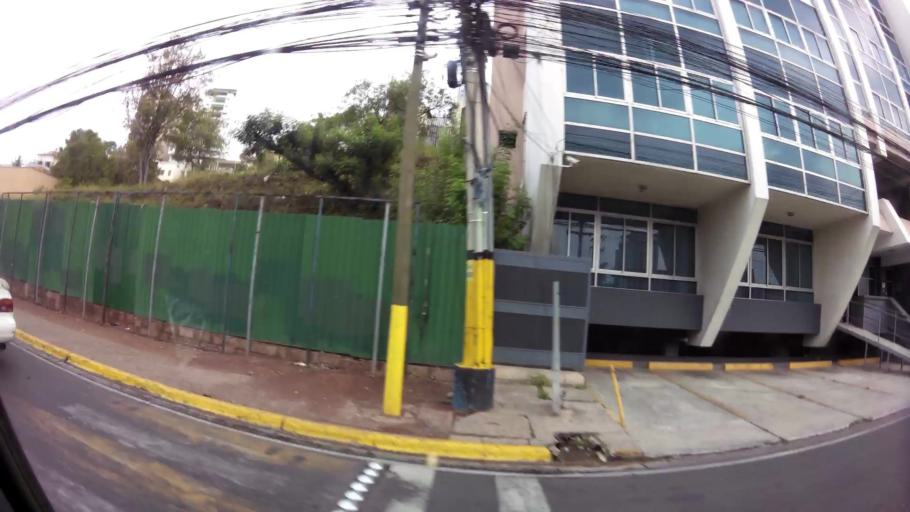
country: HN
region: Francisco Morazan
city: Tegucigalpa
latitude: 14.0895
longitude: -87.1875
